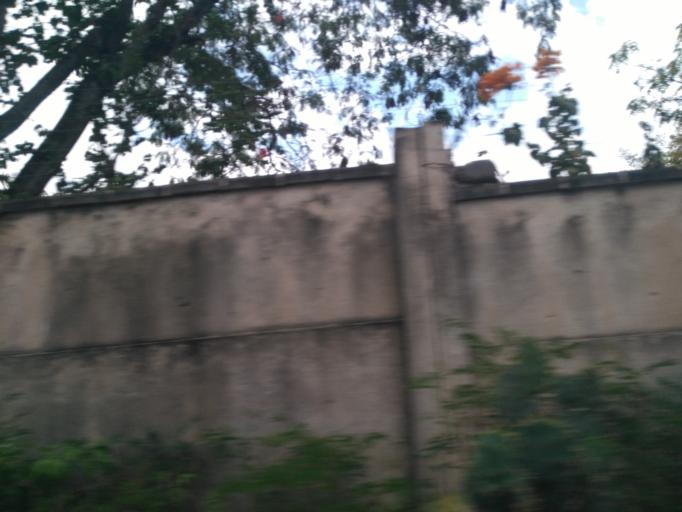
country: TZ
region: Dar es Salaam
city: Magomeni
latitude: -6.7625
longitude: 39.2741
